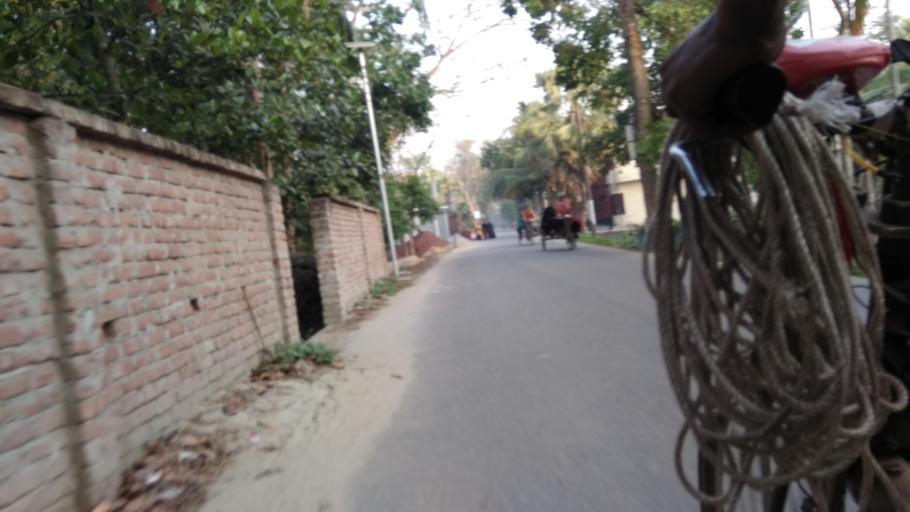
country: BD
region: Barisal
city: Mehendiganj
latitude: 22.9179
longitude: 90.4103
